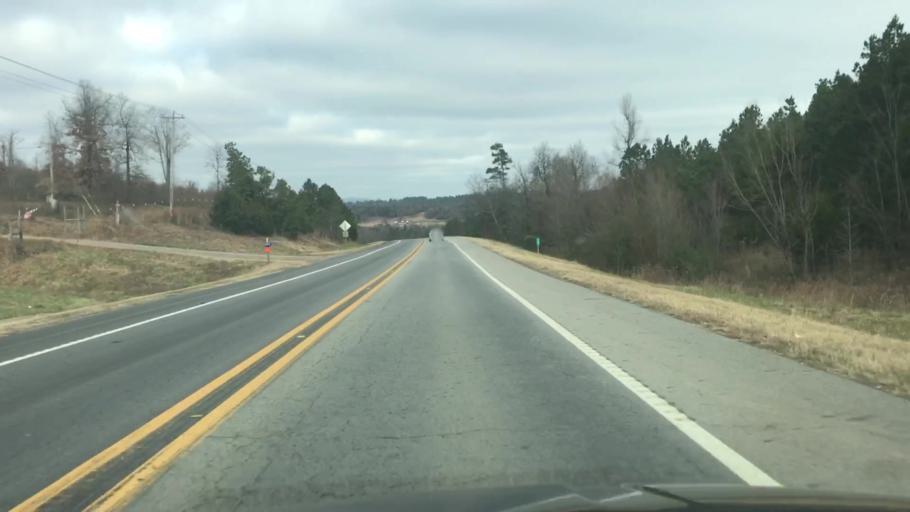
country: US
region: Arkansas
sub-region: Scott County
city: Waldron
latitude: 34.8418
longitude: -94.0539
